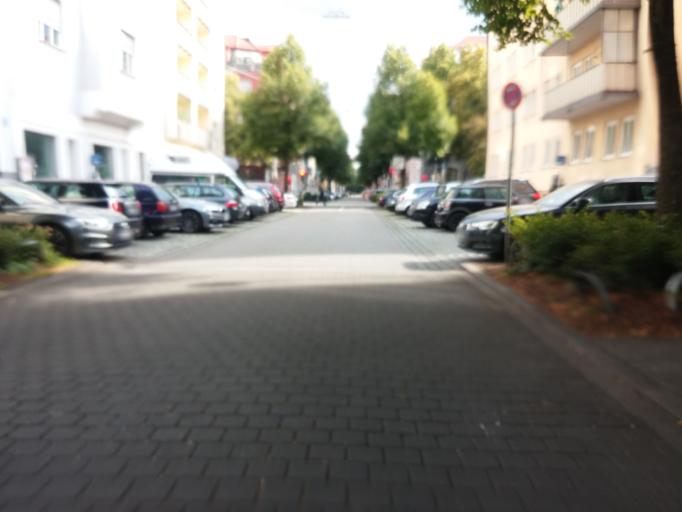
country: DE
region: Bavaria
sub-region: Upper Bavaria
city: Munich
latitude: 48.1590
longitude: 11.5726
